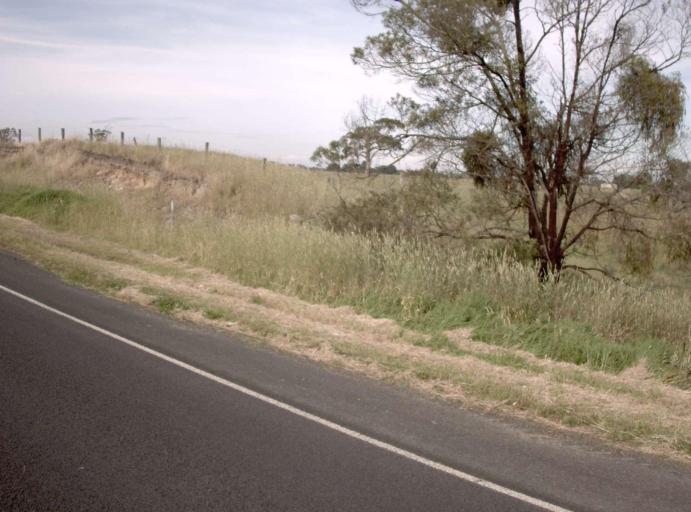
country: AU
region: Victoria
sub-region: Latrobe
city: Traralgon
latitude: -38.1498
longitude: 146.5547
